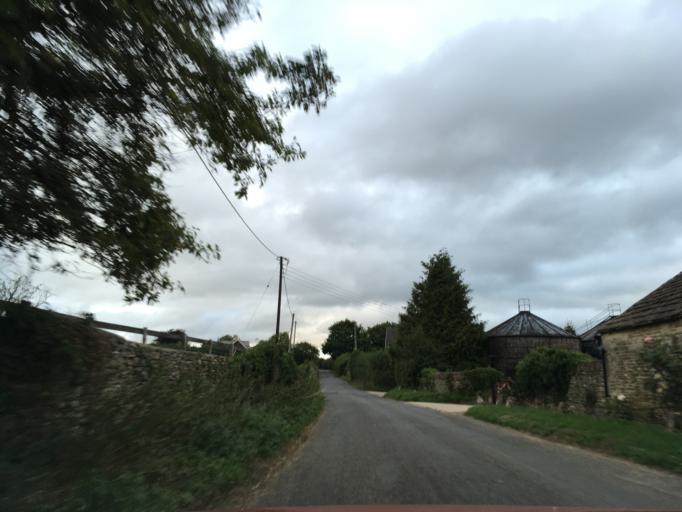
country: GB
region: England
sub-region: Wiltshire
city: Biddestone
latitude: 51.4491
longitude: -2.1992
